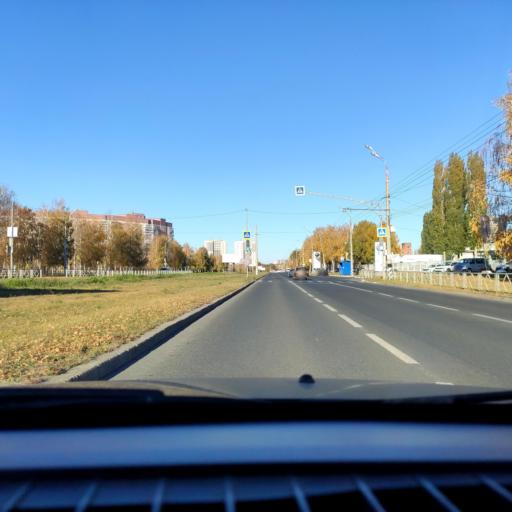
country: RU
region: Samara
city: Tol'yatti
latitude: 53.5014
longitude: 49.2645
